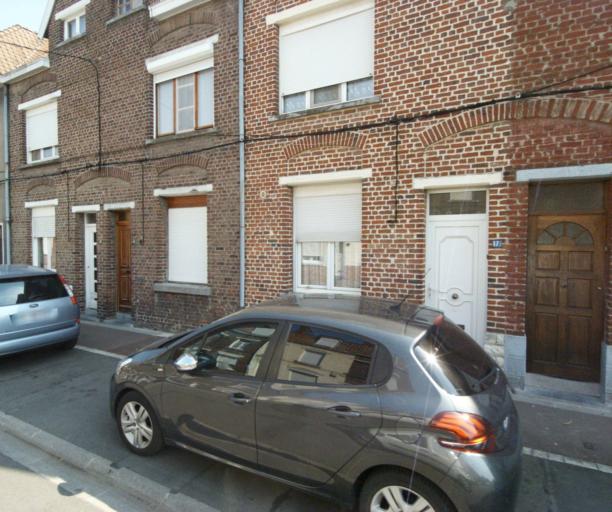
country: FR
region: Nord-Pas-de-Calais
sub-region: Departement du Nord
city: Comines
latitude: 50.7610
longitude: 3.0069
